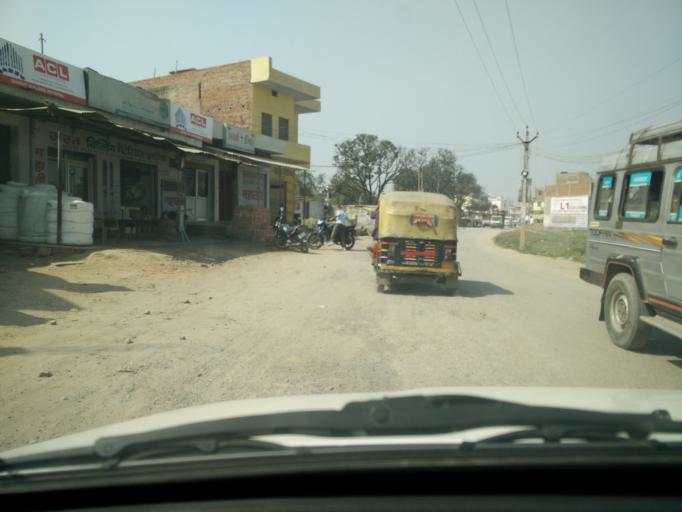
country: IN
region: Uttar Pradesh
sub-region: Varanasi
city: Ramnagar
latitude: 25.2635
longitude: 83.0183
